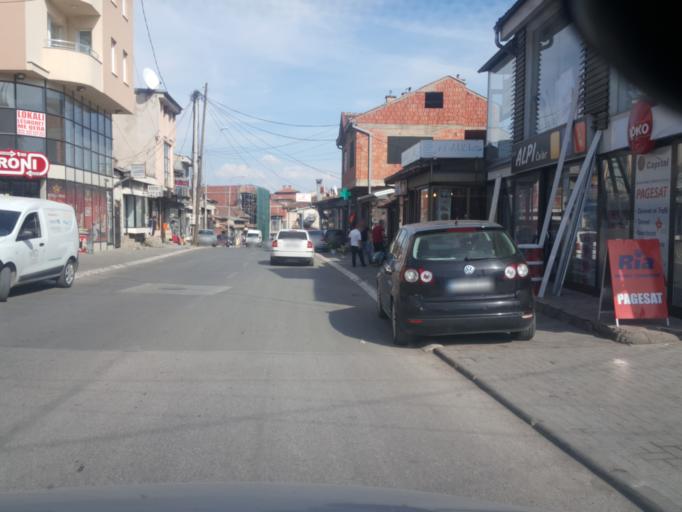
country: XK
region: Gjakova
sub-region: Komuna e Gjakoves
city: Gjakove
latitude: 42.3754
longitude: 20.4262
